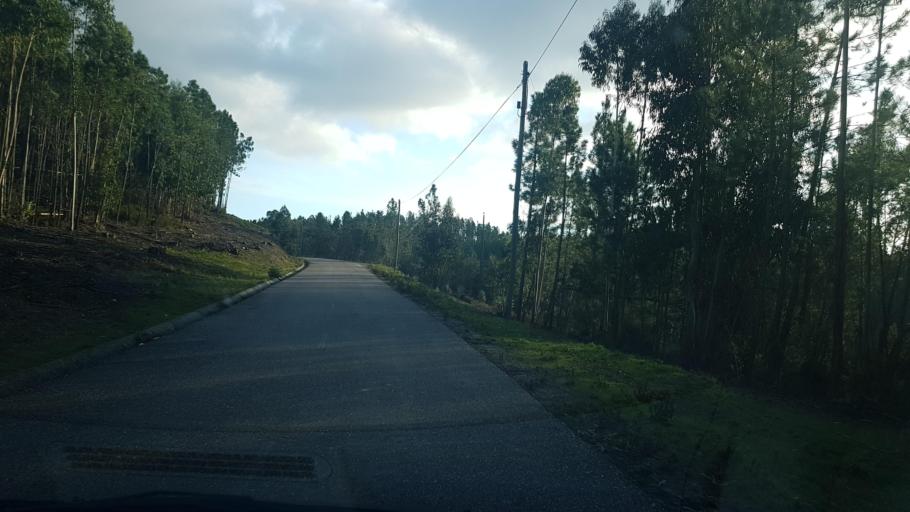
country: PT
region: Castelo Branco
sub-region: Vila de Rei
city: Vila de Rei
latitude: 39.5971
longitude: -8.1205
